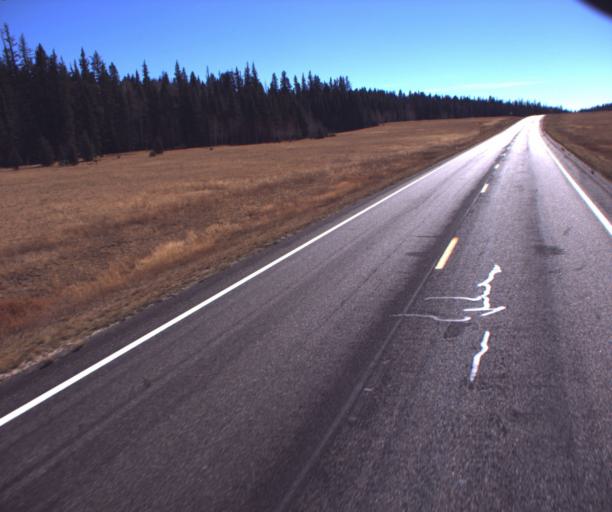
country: US
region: Arizona
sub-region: Coconino County
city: Grand Canyon
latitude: 36.3606
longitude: -112.1193
